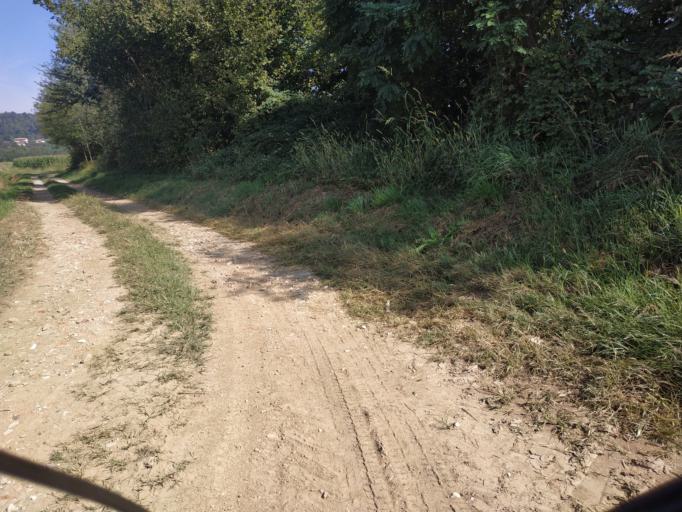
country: IT
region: Piedmont
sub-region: Provincia di Torino
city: Orio Canavese
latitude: 45.3205
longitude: 7.8506
